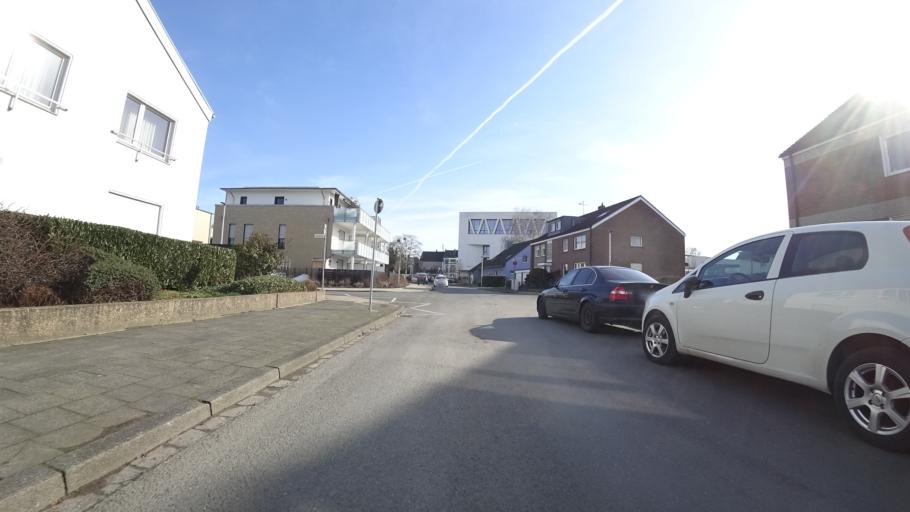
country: DE
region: North Rhine-Westphalia
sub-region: Regierungsbezirk Arnsberg
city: Hamm
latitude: 51.6850
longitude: 7.8257
